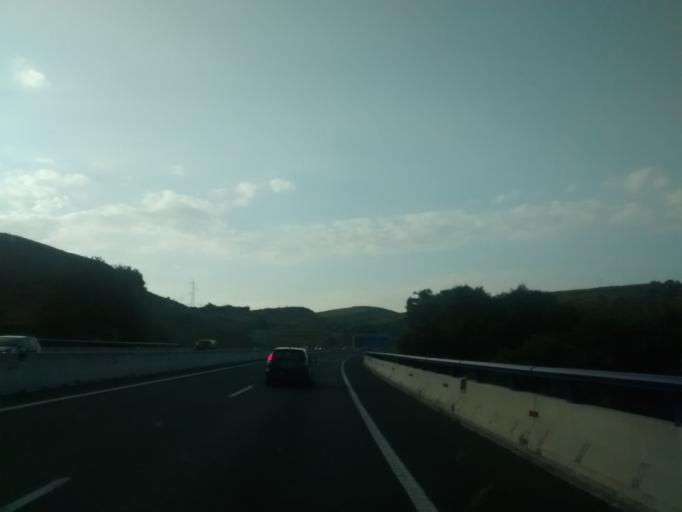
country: ES
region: Cantabria
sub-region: Provincia de Cantabria
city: Arenas de Iguna
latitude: 43.1954
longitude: -4.0712
